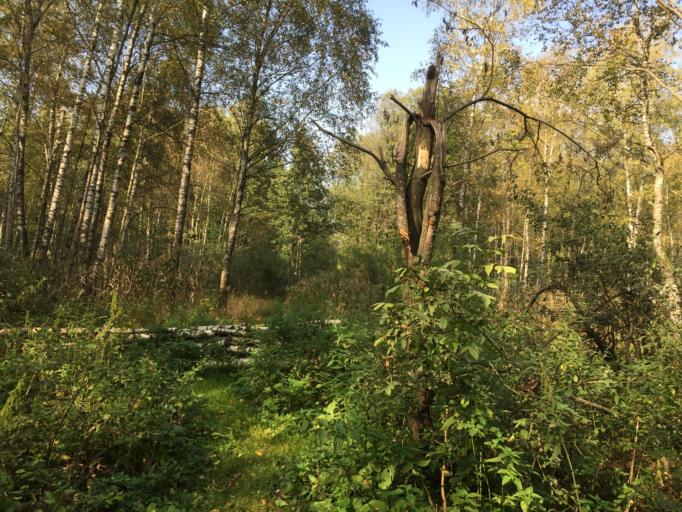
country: RU
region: Moscow
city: Babushkin
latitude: 55.8716
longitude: 37.7419
